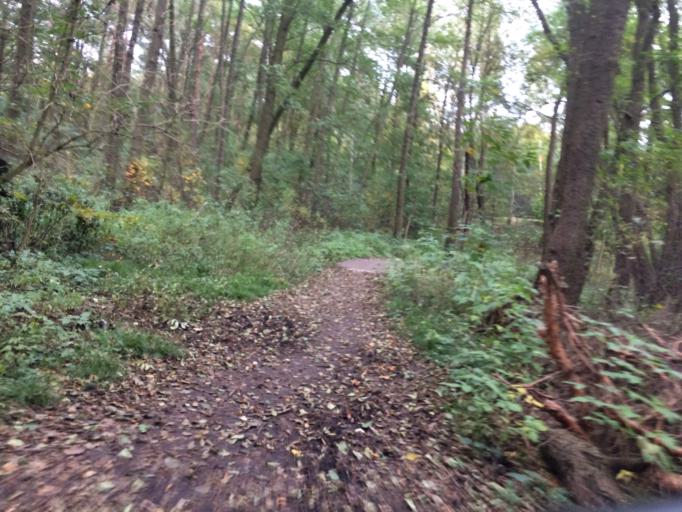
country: DE
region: Berlin
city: Blankenfelde
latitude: 52.6959
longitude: 13.3757
